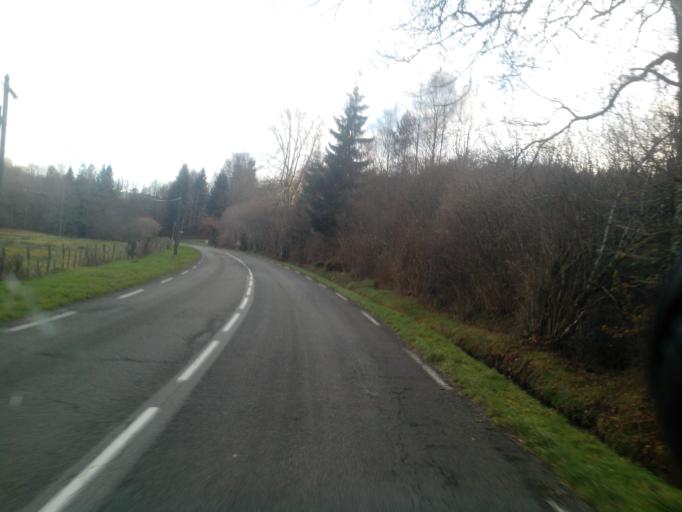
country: FR
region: Limousin
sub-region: Departement de la Haute-Vienne
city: Eymoutiers
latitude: 45.6509
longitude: 1.8215
